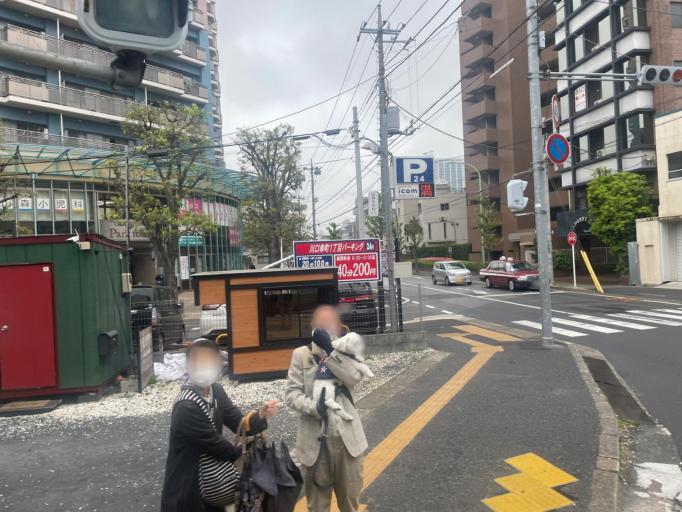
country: JP
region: Saitama
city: Kawaguchi
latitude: 35.8049
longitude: 139.7223
